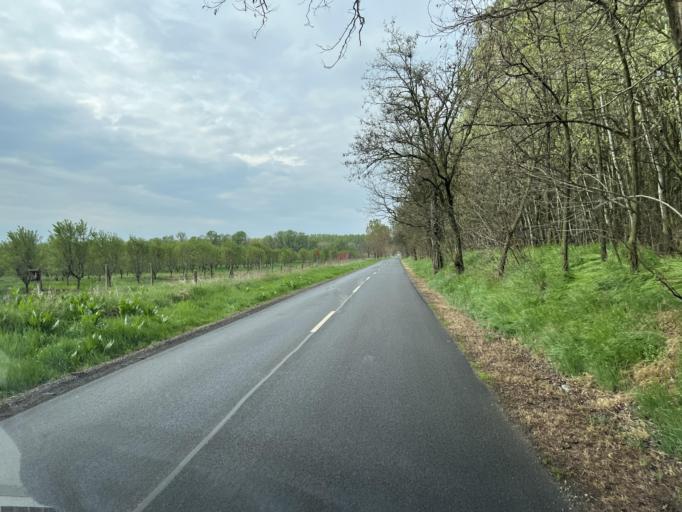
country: HU
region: Pest
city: Danszentmiklos
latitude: 47.2186
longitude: 19.5761
